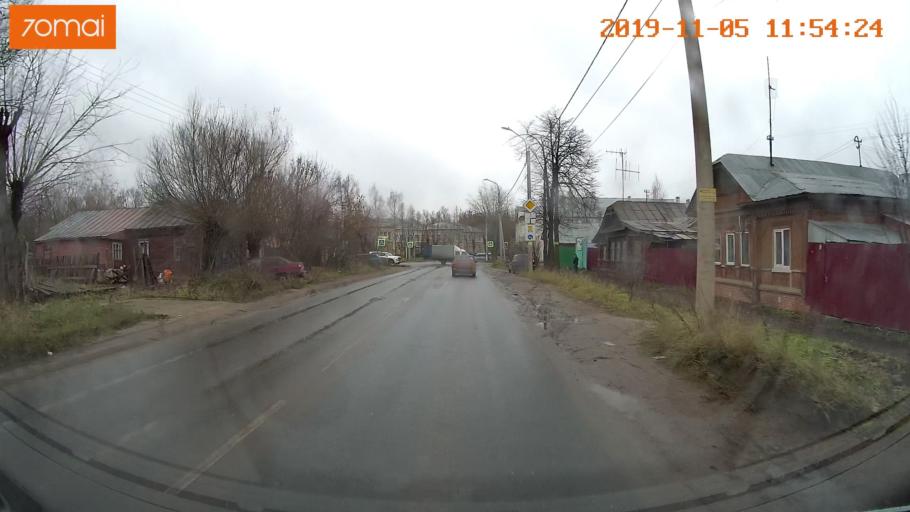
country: RU
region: Ivanovo
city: Bogorodskoye
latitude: 56.9907
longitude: 41.0314
